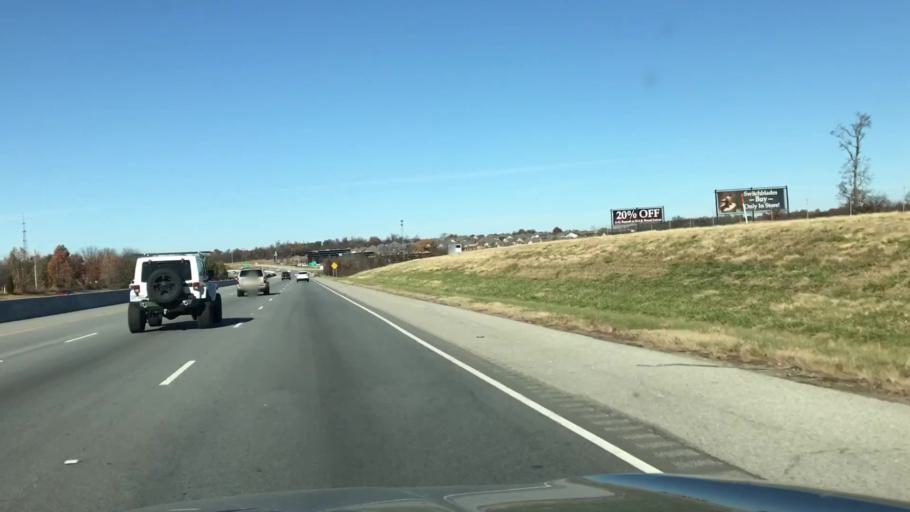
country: US
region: Arkansas
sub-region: Benton County
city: Lowell
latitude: 36.2890
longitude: -94.1611
